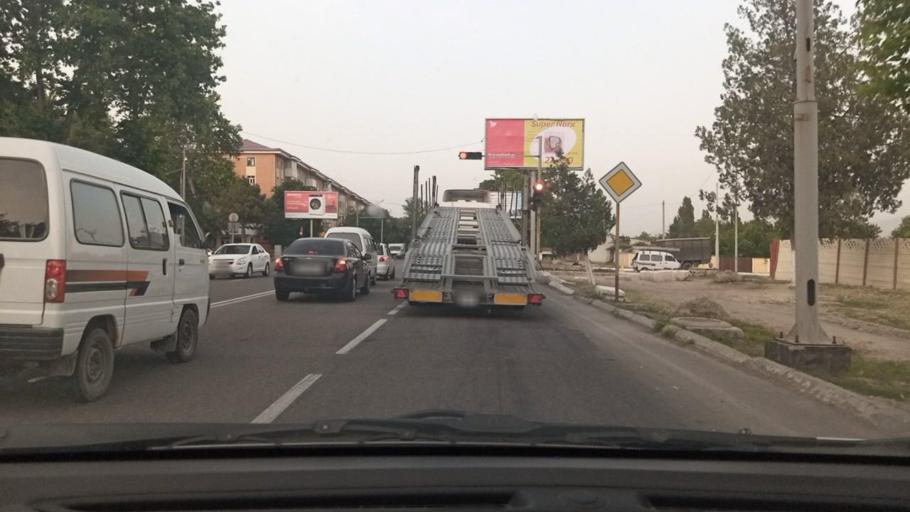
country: UZ
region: Toshkent
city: Angren
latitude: 41.0019
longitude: 70.0795
